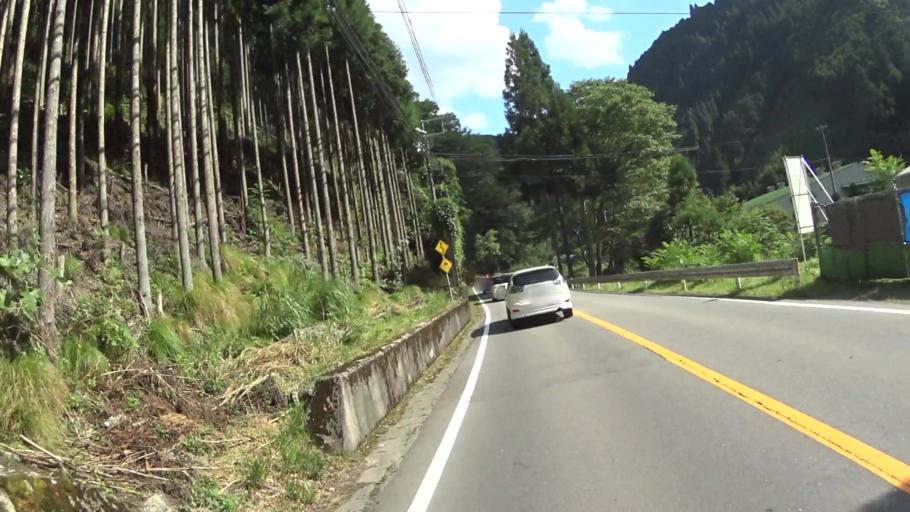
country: JP
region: Kyoto
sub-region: Kyoto-shi
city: Kamigyo-ku
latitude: 35.1006
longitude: 135.6763
